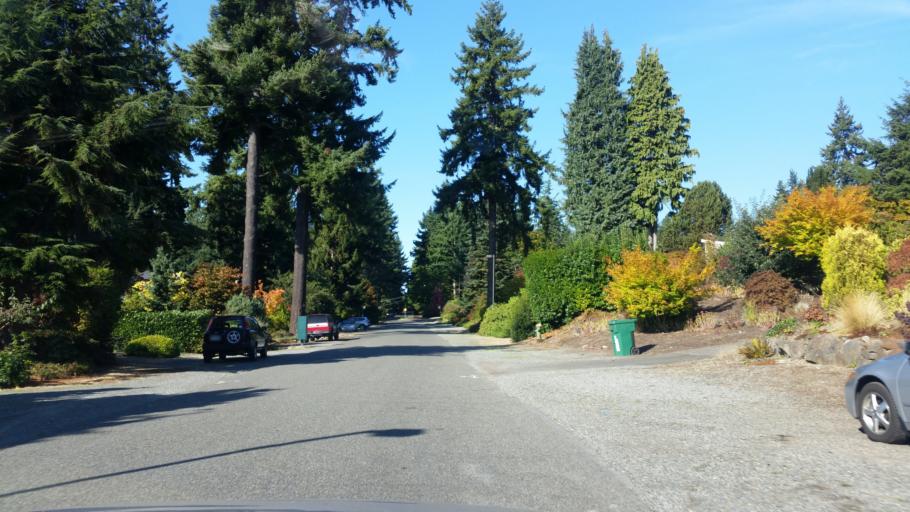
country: US
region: Washington
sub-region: King County
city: Shoreline
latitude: 47.7237
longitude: -122.3664
